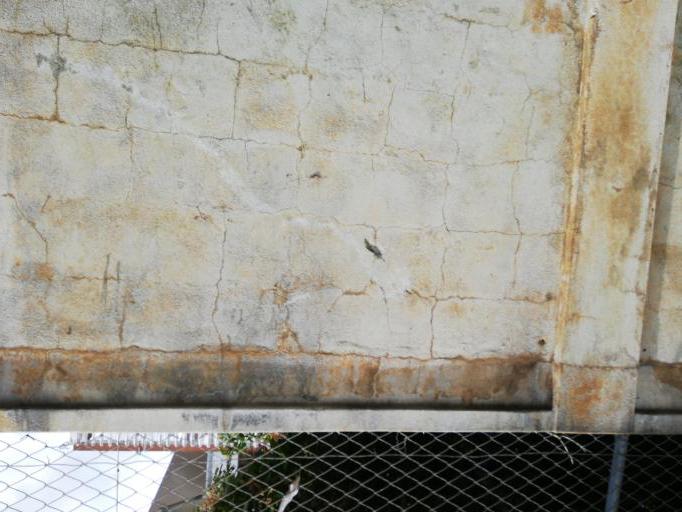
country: MU
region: Moka
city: Pailles
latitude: -20.2023
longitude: 57.4723
